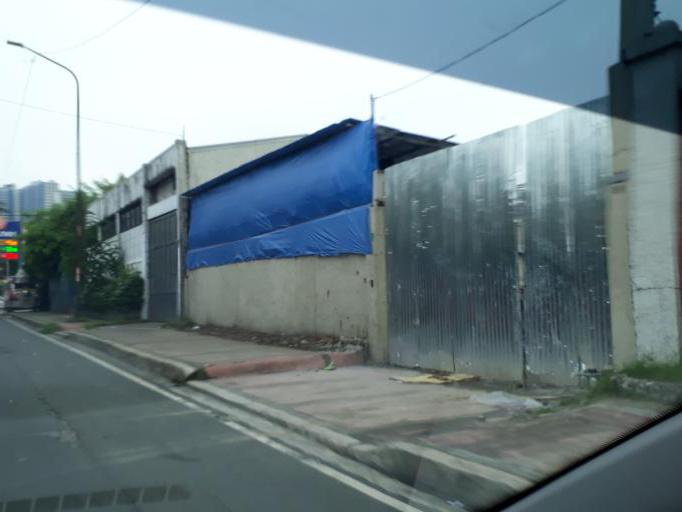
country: PH
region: Calabarzon
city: Del Monte
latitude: 14.6254
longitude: 120.9981
